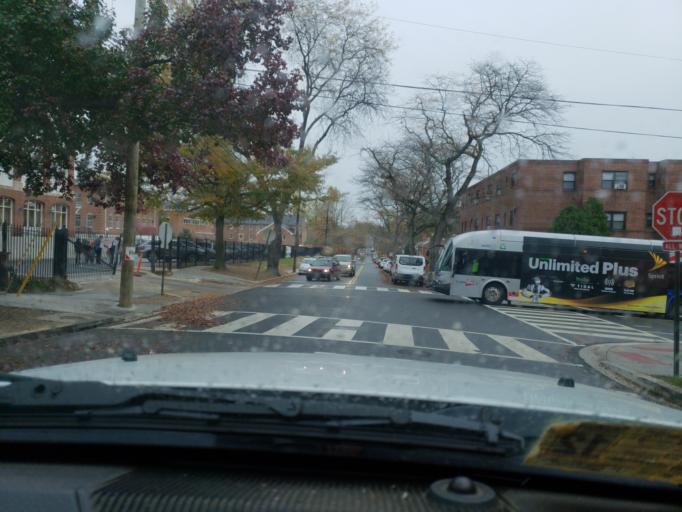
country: US
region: Maryland
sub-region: Montgomery County
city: Silver Spring
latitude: 38.9723
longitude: -77.0337
